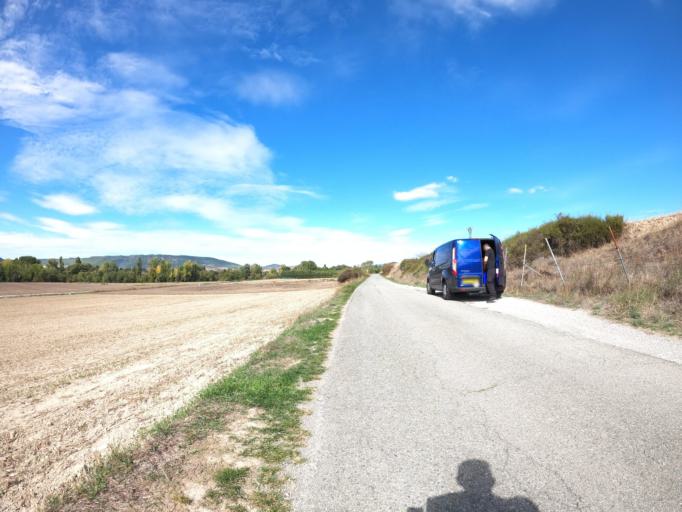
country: ES
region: Navarre
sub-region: Provincia de Navarra
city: Lumbier
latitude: 42.6406
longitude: -1.3099
